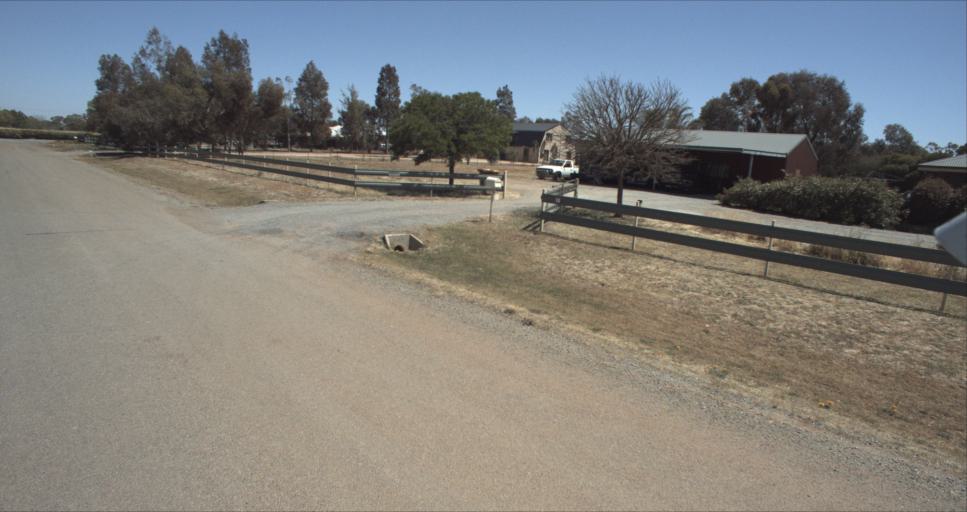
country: AU
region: New South Wales
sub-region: Leeton
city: Leeton
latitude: -34.5309
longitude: 146.3957
